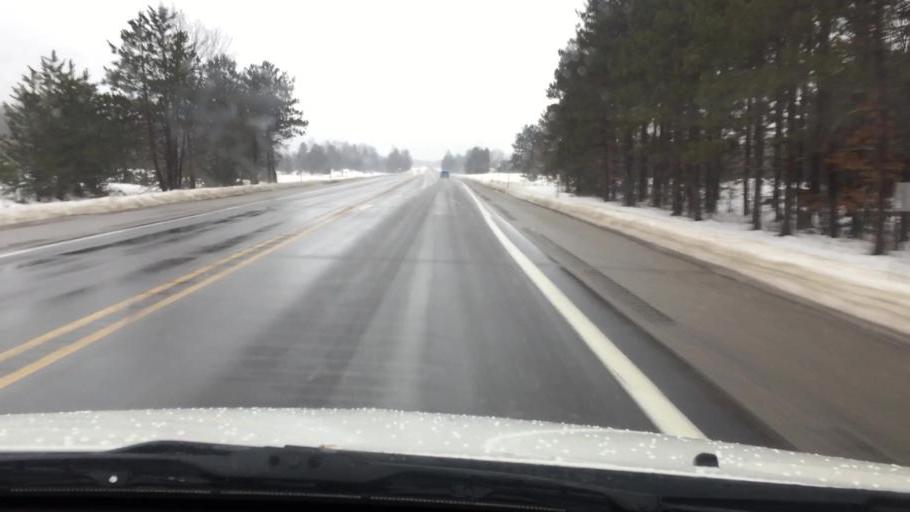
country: US
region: Michigan
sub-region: Kalkaska County
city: Kalkaska
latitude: 44.6821
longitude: -85.2263
